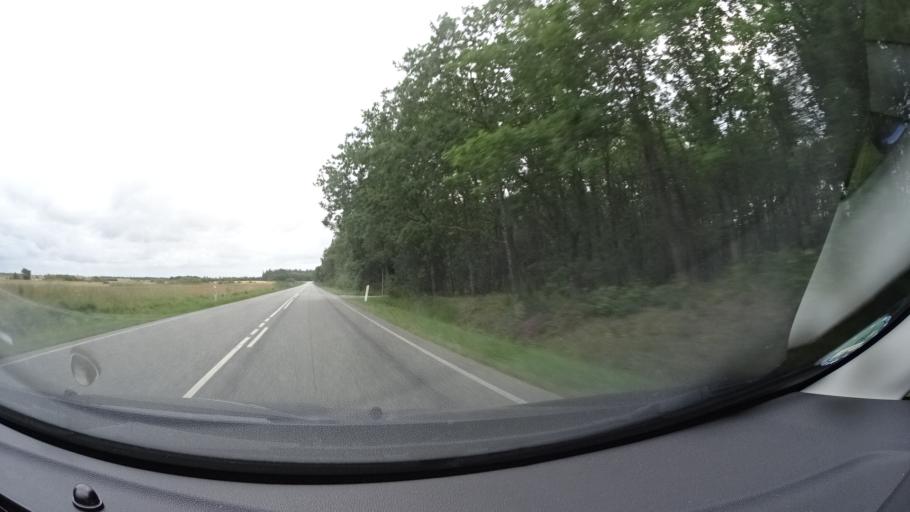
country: DK
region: Central Jutland
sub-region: Holstebro Kommune
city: Ulfborg
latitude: 56.2959
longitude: 8.1889
